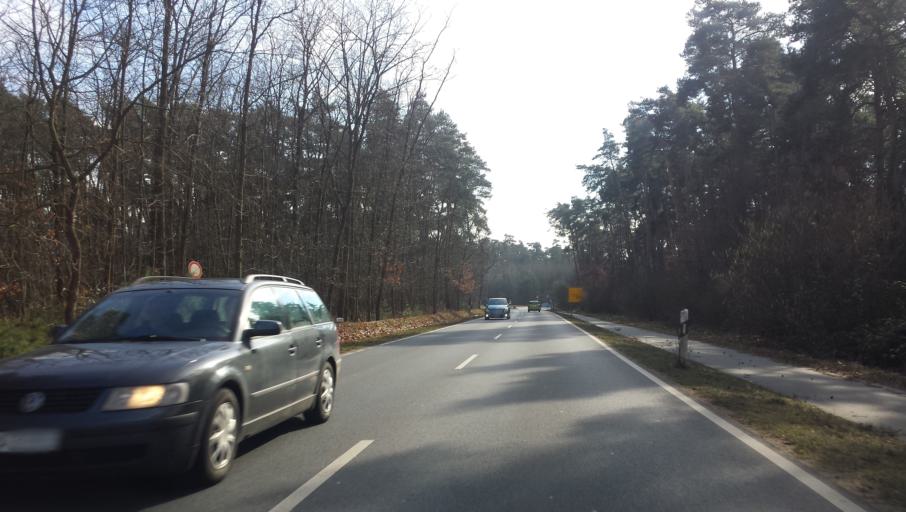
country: DE
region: Hesse
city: Weiterstadt
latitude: 49.9149
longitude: 8.6160
